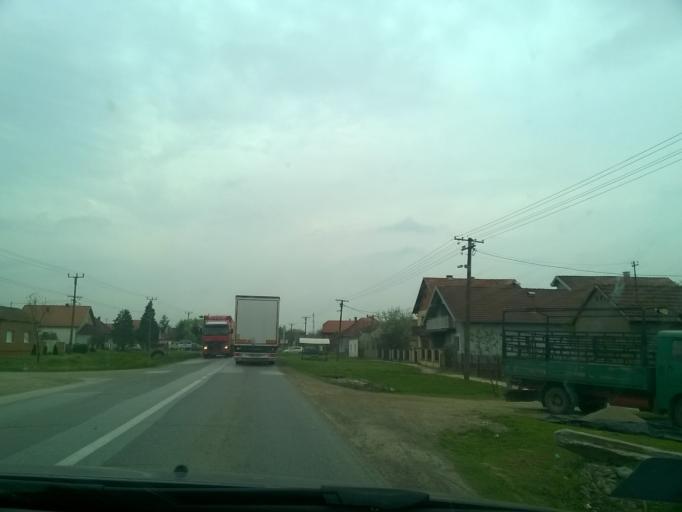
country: RS
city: Hrtkovci
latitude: 44.8895
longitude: 19.7638
